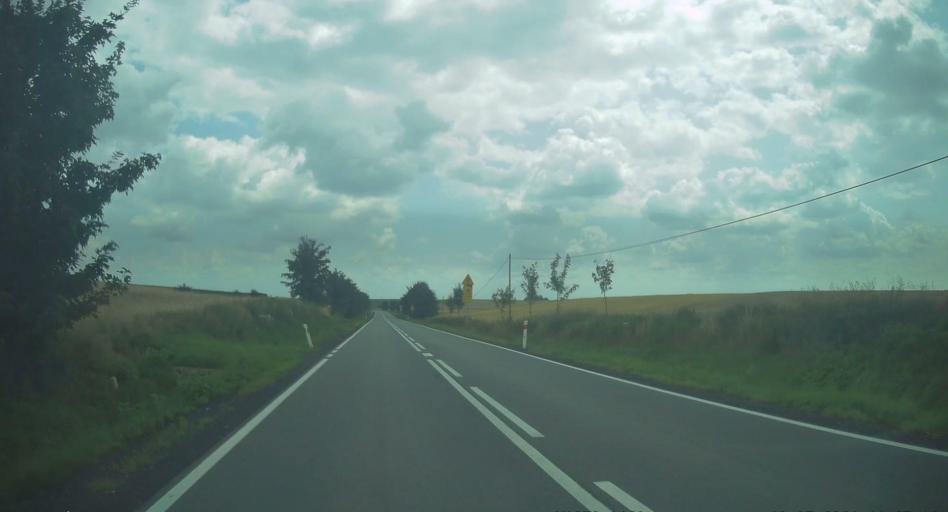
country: PL
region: Opole Voivodeship
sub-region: Powiat prudnicki
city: Raclawice Slaskie
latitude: 50.3536
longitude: 17.8012
